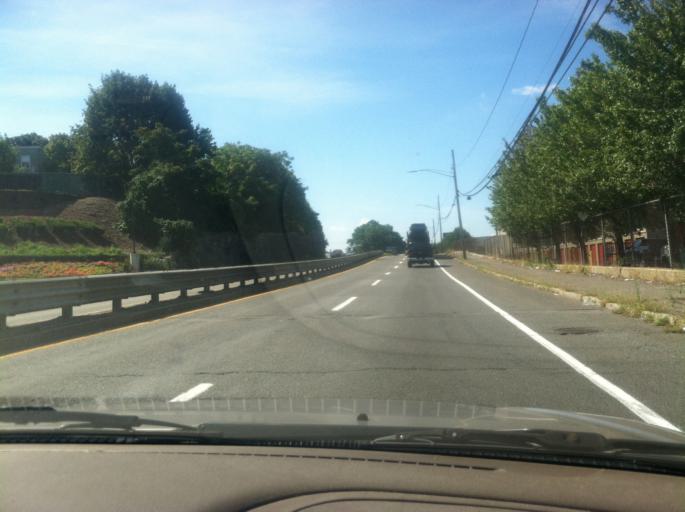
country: US
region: Massachusetts
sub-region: Suffolk County
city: Revere
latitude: 42.3912
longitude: -71.0129
